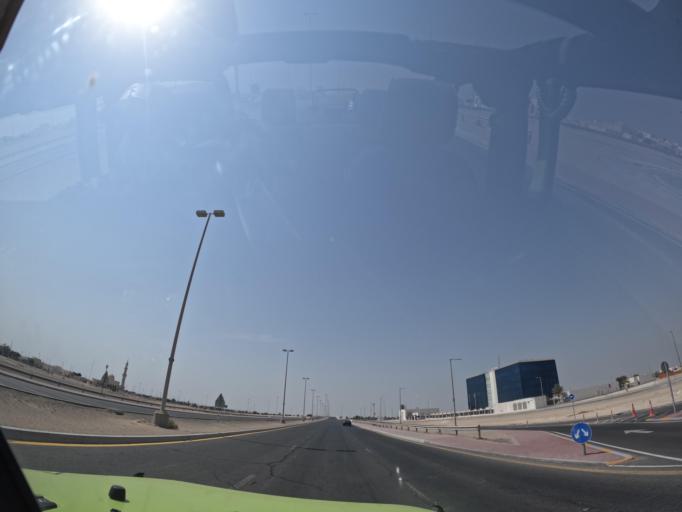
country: AE
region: Abu Dhabi
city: Abu Dhabi
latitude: 24.3367
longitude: 54.6418
